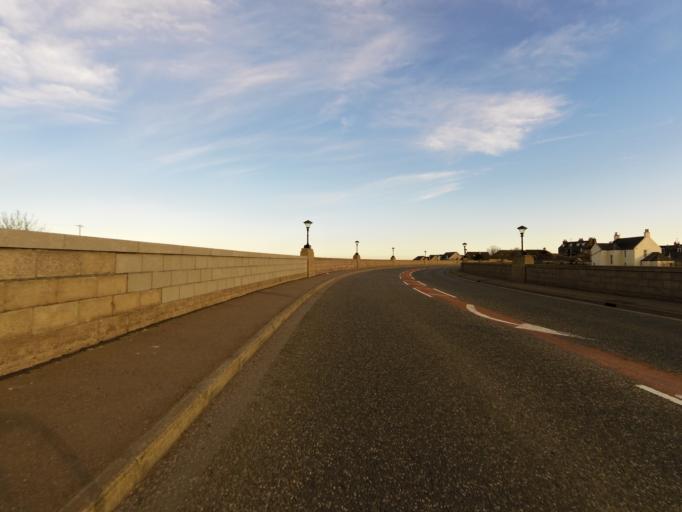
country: GB
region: Scotland
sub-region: Aberdeenshire
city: Inverbervie
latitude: 56.8473
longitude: -2.2772
